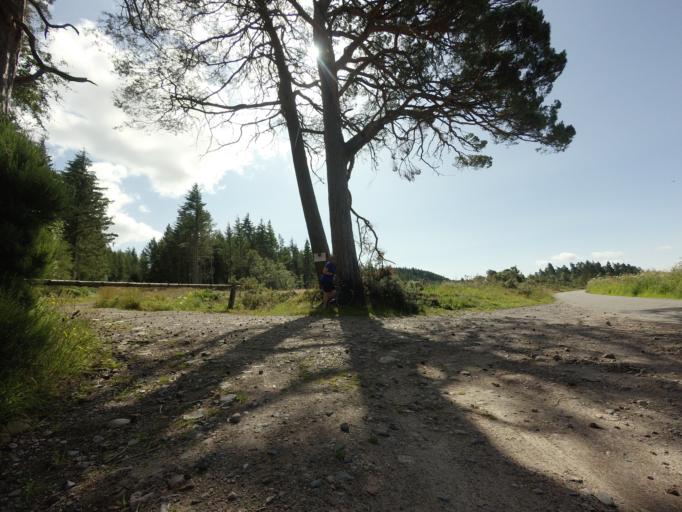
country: GB
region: Scotland
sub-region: Highland
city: Nairn
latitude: 57.5305
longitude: -3.8619
